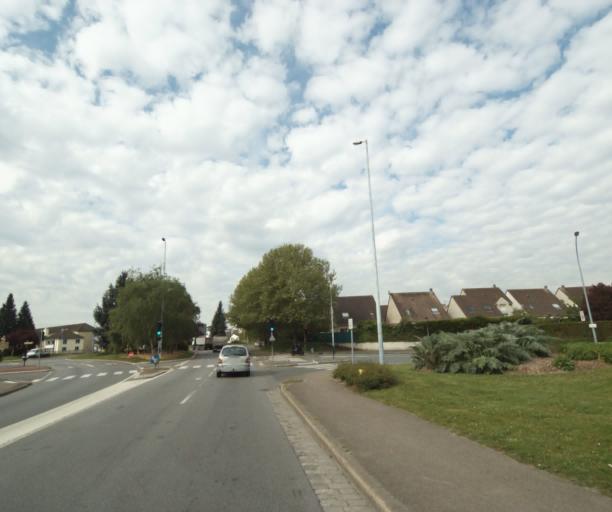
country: FR
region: Ile-de-France
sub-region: Departement des Yvelines
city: Les Mureaux
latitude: 48.9978
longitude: 1.9141
